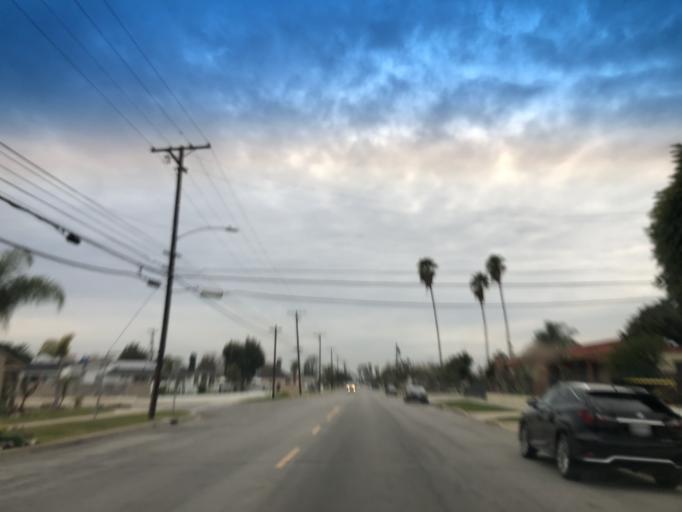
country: US
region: California
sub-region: Los Angeles County
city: Azusa
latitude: 34.1180
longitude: -117.9131
